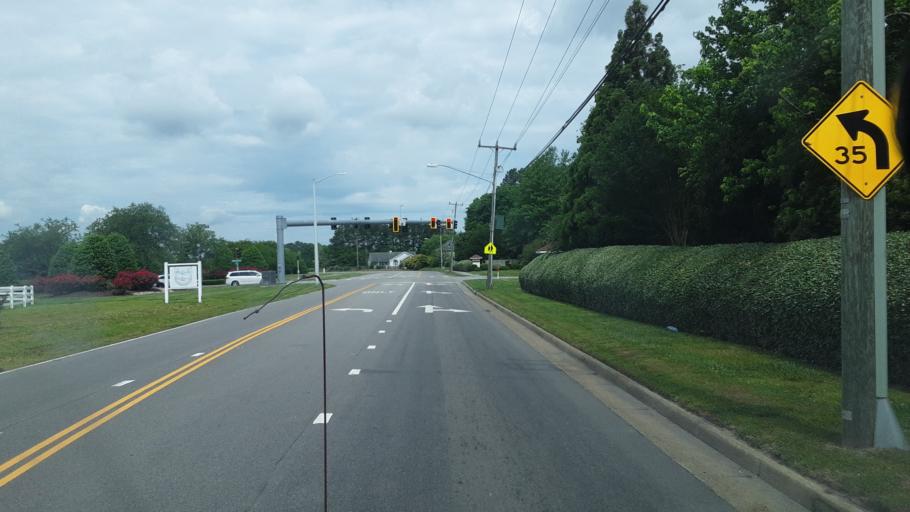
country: US
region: Virginia
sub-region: City of Virginia Beach
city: Virginia Beach
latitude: 36.7460
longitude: -75.9954
